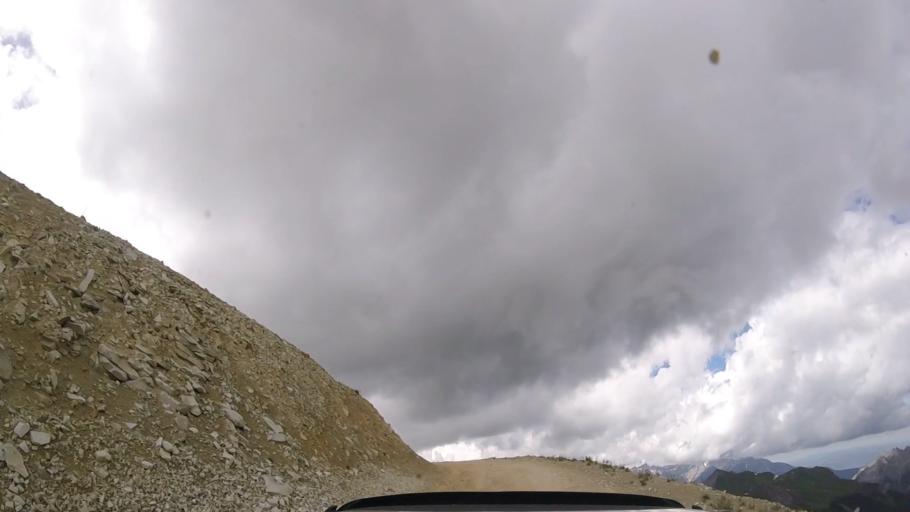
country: US
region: Colorado
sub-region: Ouray County
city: Ouray
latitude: 37.9730
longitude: -107.5872
